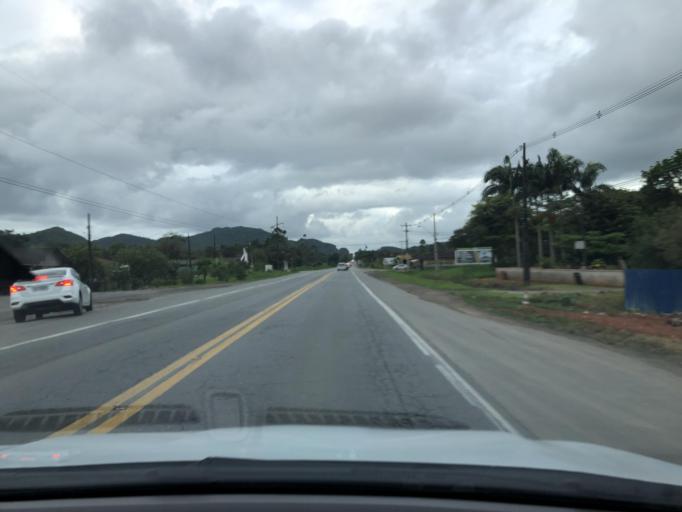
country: BR
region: Santa Catarina
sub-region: Sao Francisco Do Sul
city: Sao Francisco do Sul
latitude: -26.3371
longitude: -48.6542
